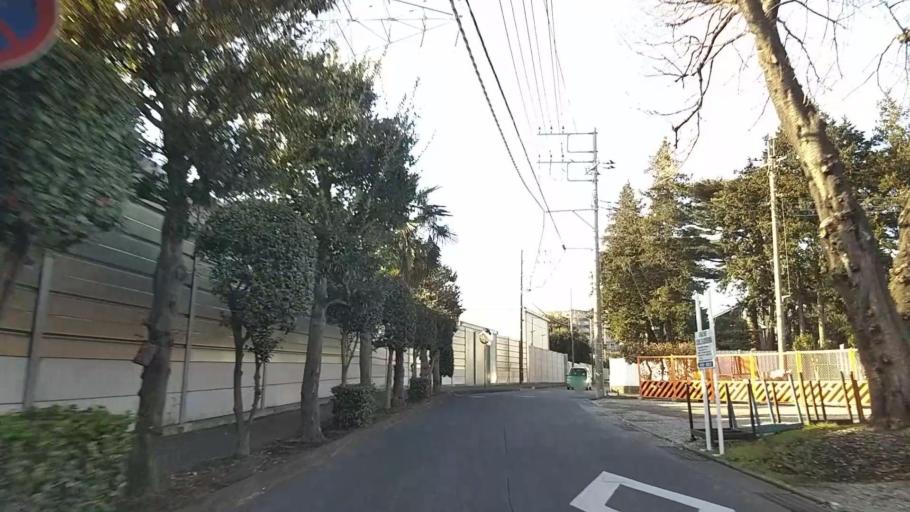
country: JP
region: Kanagawa
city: Atsugi
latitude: 35.4525
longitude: 139.3364
